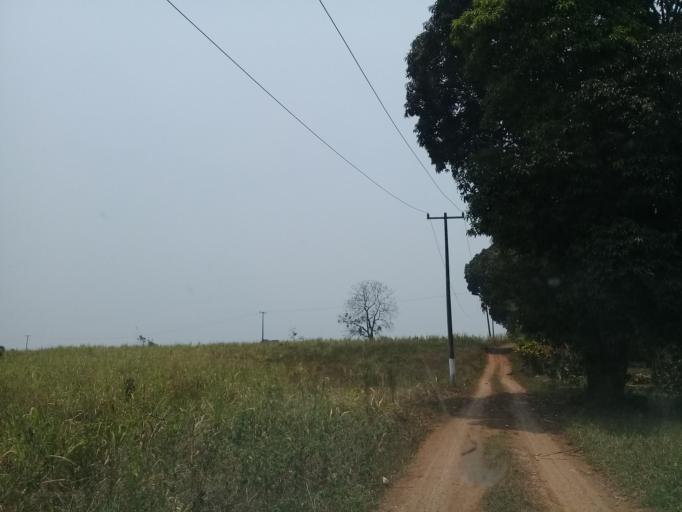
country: MX
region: Veracruz
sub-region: Tezonapa
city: Laguna Chica (Pueblo Nuevo)
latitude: 18.5383
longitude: -96.7313
